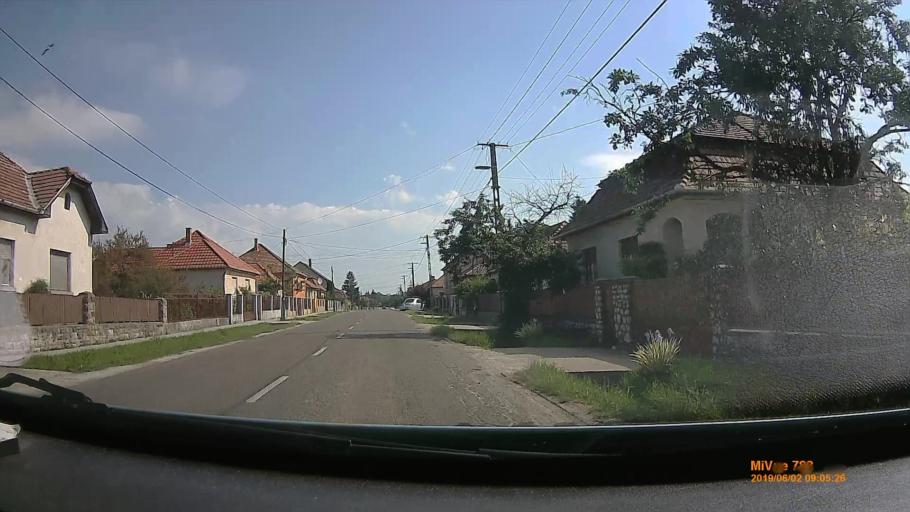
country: HU
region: Borsod-Abauj-Zemplen
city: Kazincbarcika
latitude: 48.1776
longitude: 20.6488
